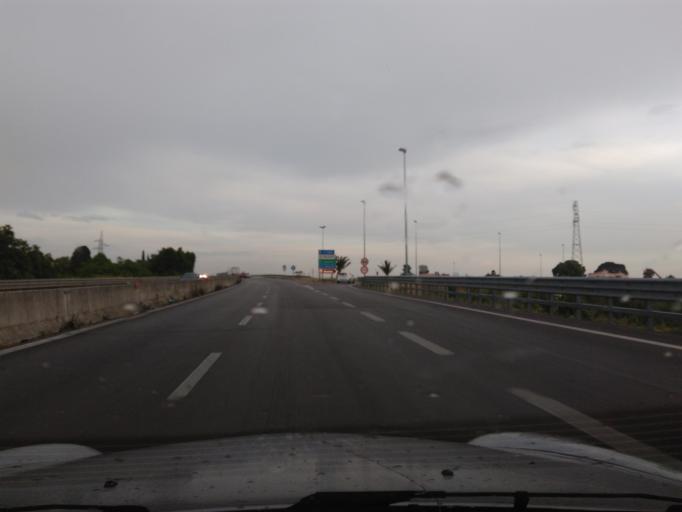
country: IT
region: Apulia
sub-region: Provincia di Bari
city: Molfetta
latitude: 41.1883
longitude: 16.5841
